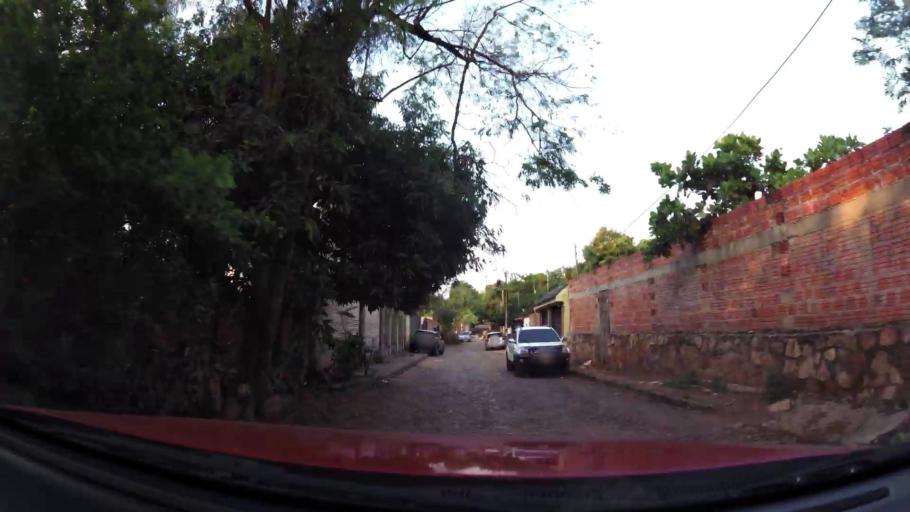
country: PY
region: Central
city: Lambare
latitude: -25.3535
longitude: -57.5999
